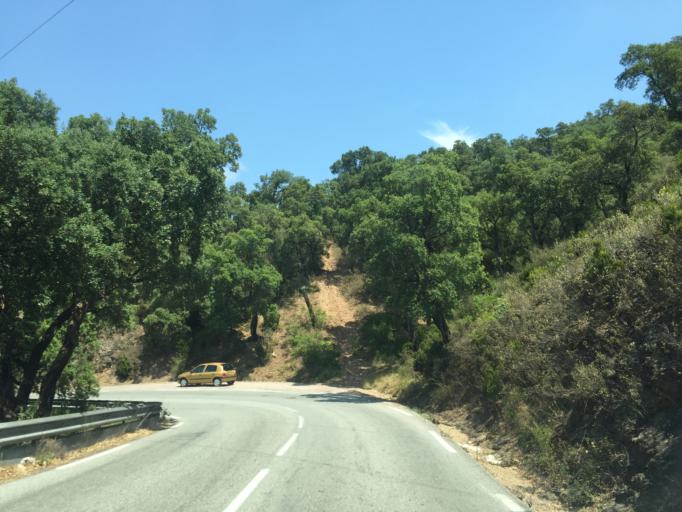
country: FR
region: Provence-Alpes-Cote d'Azur
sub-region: Departement du Var
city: Sainte-Maxime
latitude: 43.3654
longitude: 6.6742
